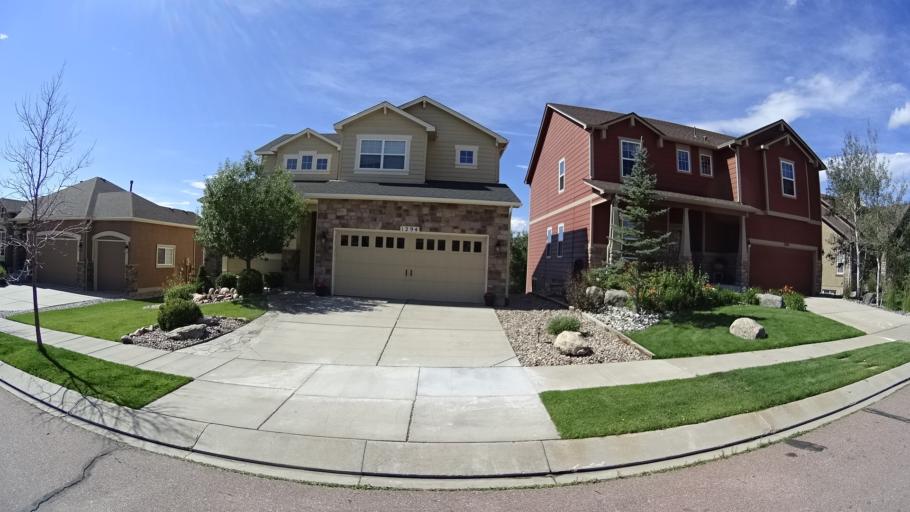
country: US
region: Colorado
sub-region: El Paso County
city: Gleneagle
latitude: 39.0266
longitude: -104.8091
